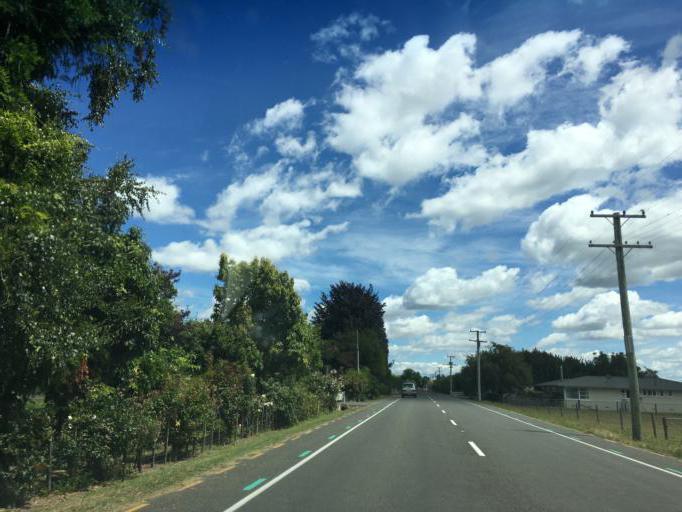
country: NZ
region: Hawke's Bay
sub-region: Hastings District
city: Hastings
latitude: -39.6551
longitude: 176.8710
